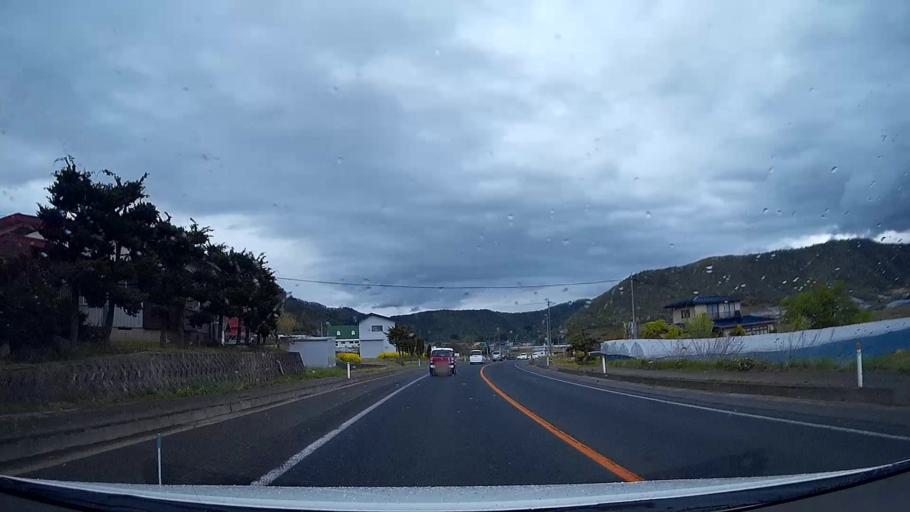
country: JP
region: Yamagata
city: Takahata
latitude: 38.0765
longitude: 140.1831
